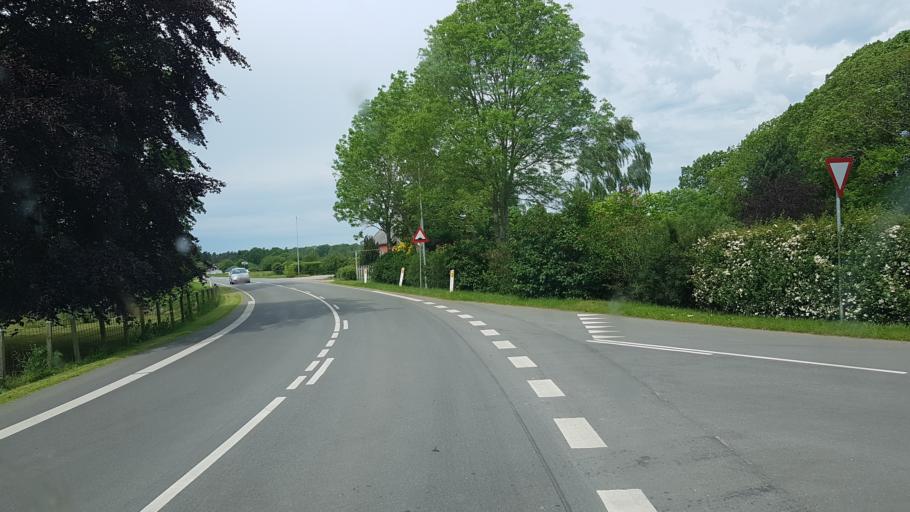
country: DK
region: South Denmark
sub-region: Nordfyns Kommune
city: Sonderso
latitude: 55.5617
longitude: 10.2314
